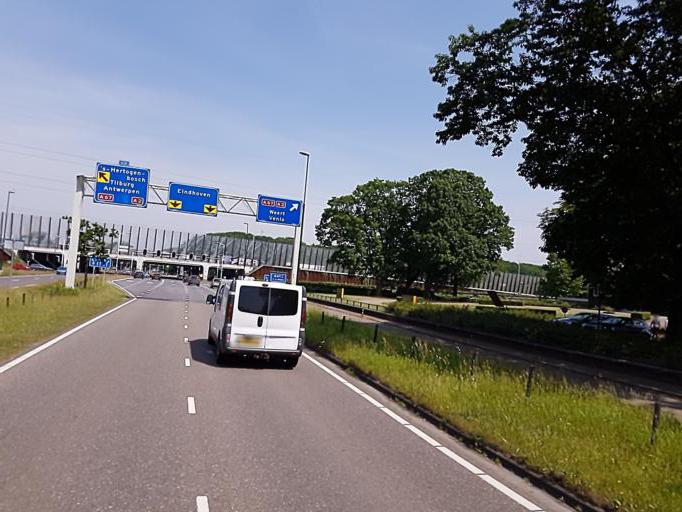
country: NL
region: North Brabant
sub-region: Gemeente Eindhoven
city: Eindhoven
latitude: 51.4035
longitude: 5.4803
